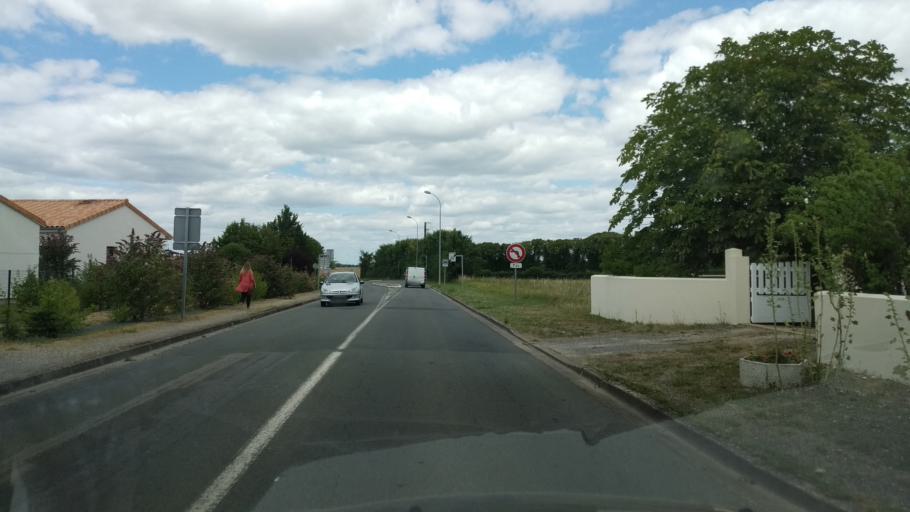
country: FR
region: Poitou-Charentes
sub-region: Departement de la Vienne
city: Avanton
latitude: 46.6648
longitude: 0.3046
